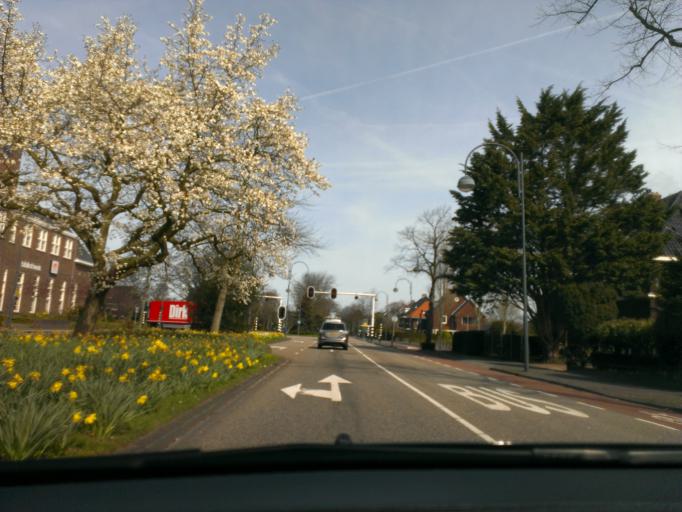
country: NL
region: North Holland
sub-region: Gemeente Heemstede
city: Heemstede
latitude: 52.3521
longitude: 4.6246
